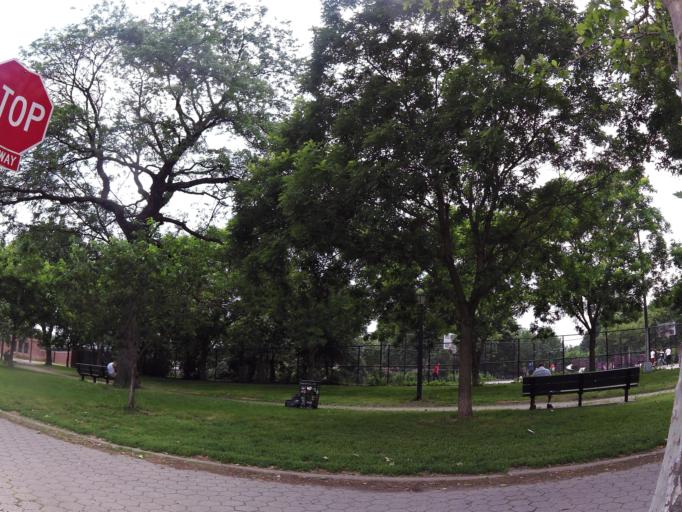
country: US
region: New York
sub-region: Queens County
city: Long Island City
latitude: 40.7214
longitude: -73.9490
